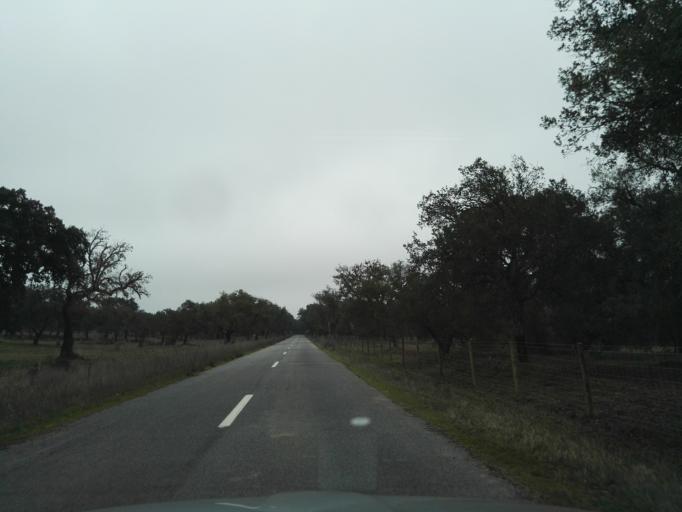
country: PT
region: Evora
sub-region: Vendas Novas
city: Vendas Novas
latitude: 38.7670
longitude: -8.3833
